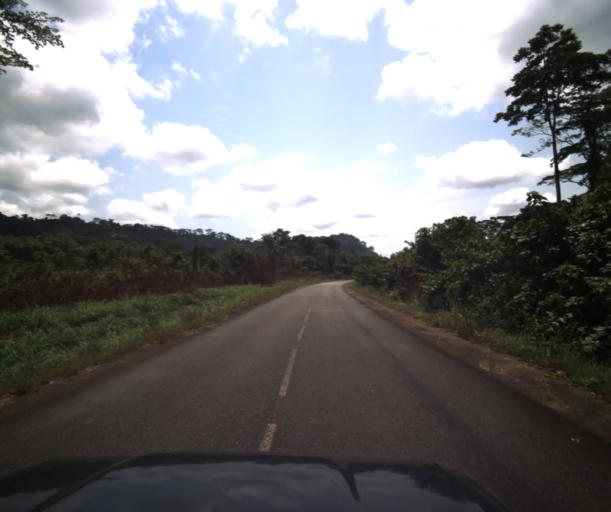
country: CM
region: Centre
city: Eseka
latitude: 3.8037
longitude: 10.8149
